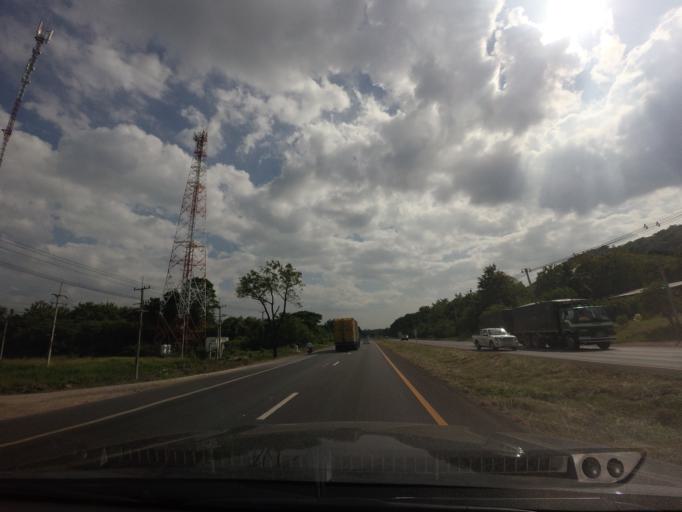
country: TH
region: Lop Buri
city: Chai Badan
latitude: 15.2887
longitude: 101.1268
